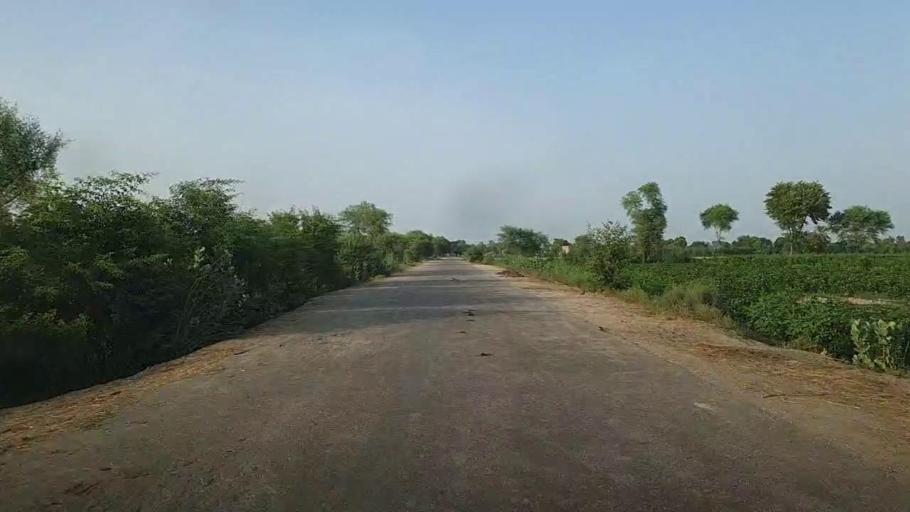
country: PK
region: Sindh
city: Ubauro
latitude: 28.1292
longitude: 69.8322
